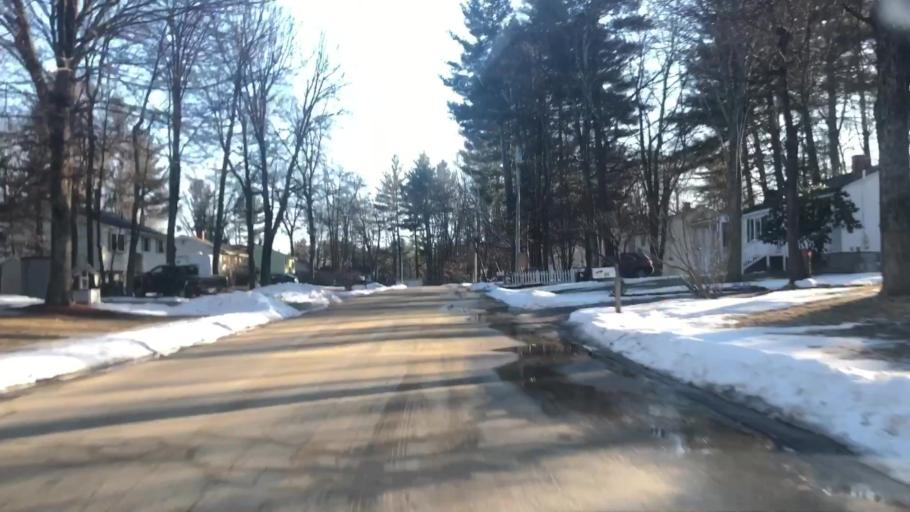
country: US
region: New Hampshire
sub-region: Hillsborough County
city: Milford
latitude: 42.8348
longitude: -71.6723
